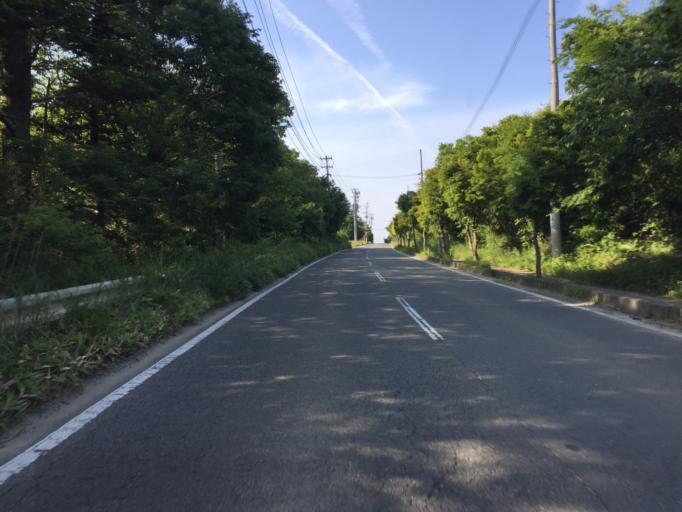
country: JP
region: Fukushima
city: Namie
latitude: 37.6721
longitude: 141.0024
